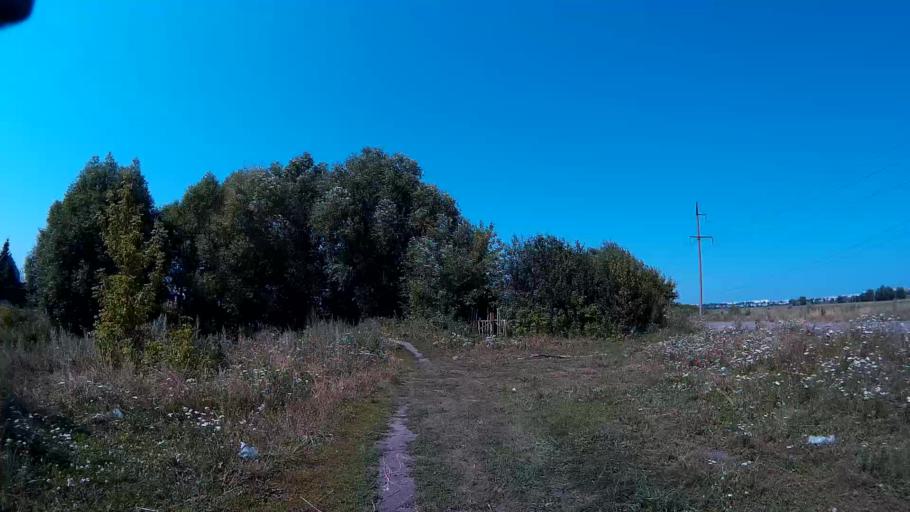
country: RU
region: Ulyanovsk
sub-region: Ulyanovskiy Rayon
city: Ulyanovsk
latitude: 54.2380
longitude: 48.2663
